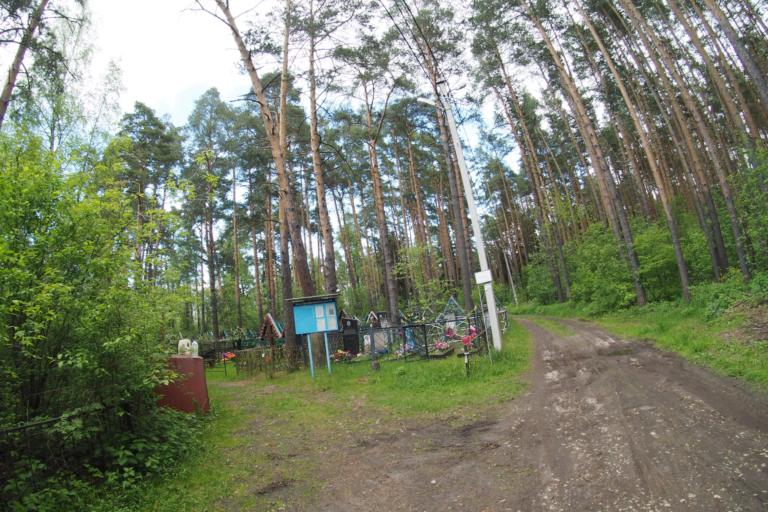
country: RU
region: Moskovskaya
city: Rechitsy
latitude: 55.5398
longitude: 38.4361
